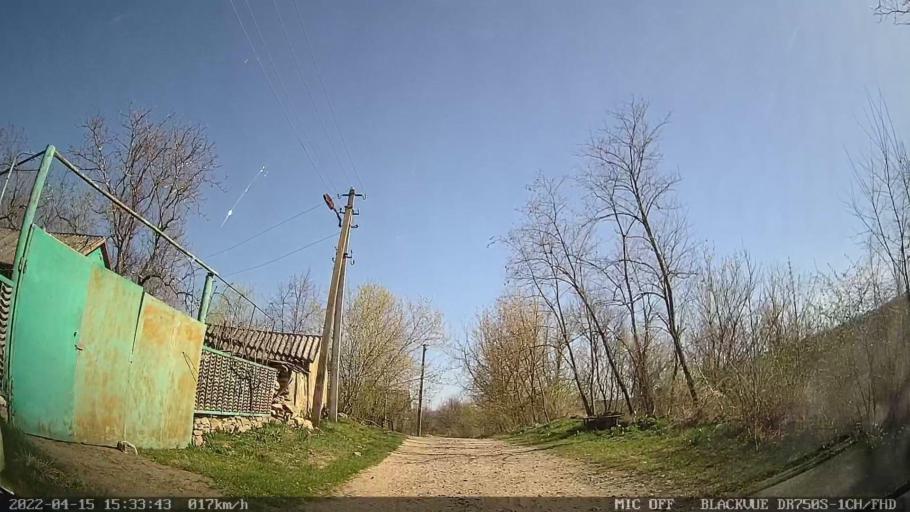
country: MD
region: Raionul Ocnita
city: Otaci
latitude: 48.3490
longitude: 27.9245
